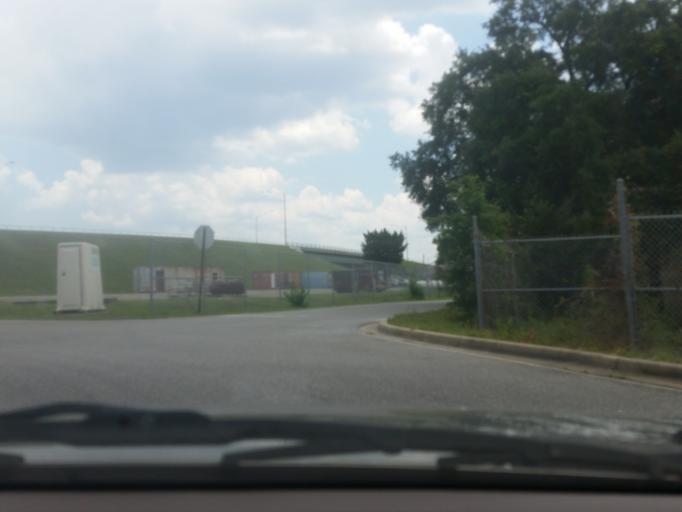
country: US
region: Florida
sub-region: Escambia County
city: Pensacola
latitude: 30.4128
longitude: -87.2447
